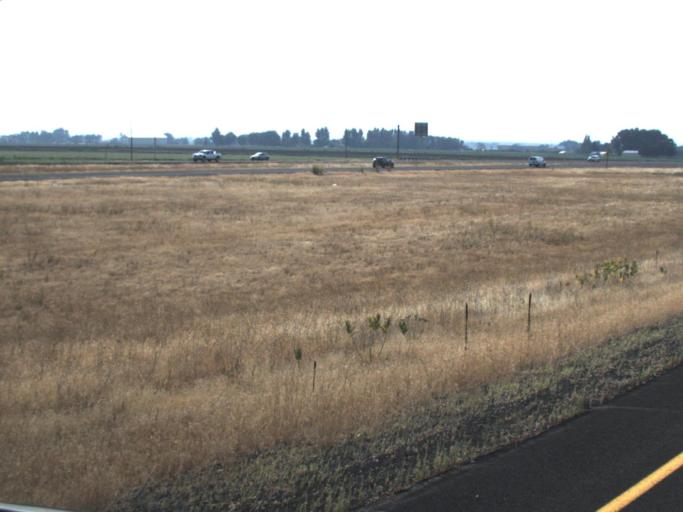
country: US
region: Washington
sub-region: Kittitas County
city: Ellensburg
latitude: 46.9661
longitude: -120.5100
